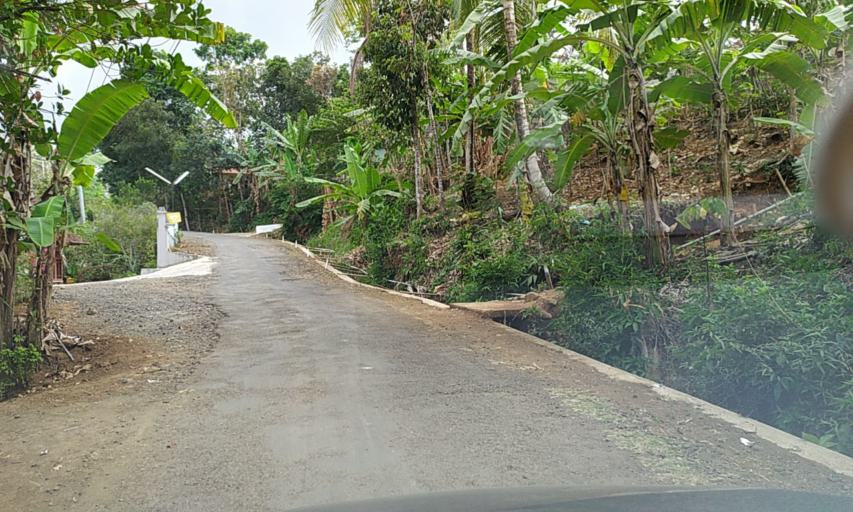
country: ID
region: Central Java
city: Kubang
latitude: -7.2893
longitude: 108.6300
